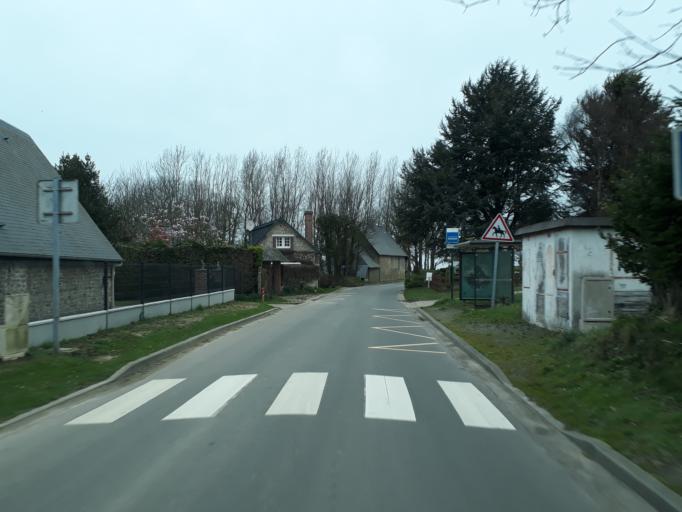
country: FR
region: Haute-Normandie
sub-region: Departement de la Seine-Maritime
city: Les Loges
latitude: 49.7220
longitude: 0.2800
